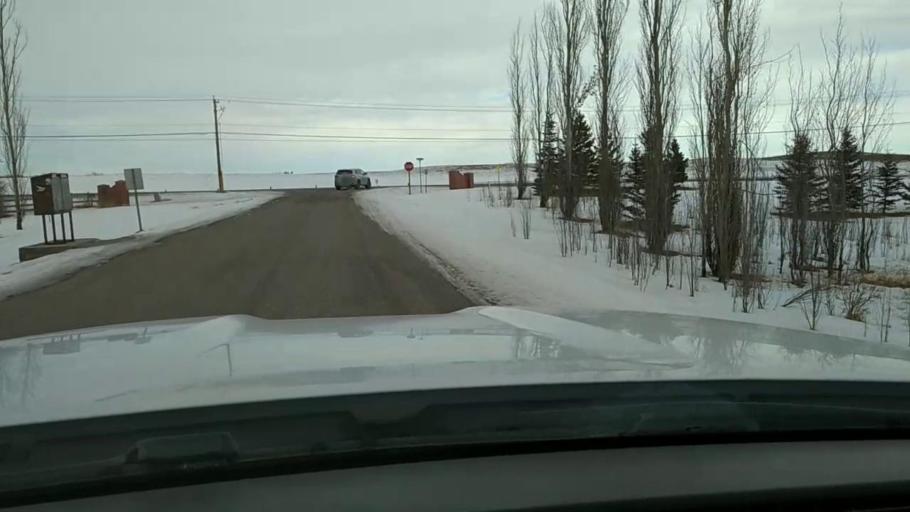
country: CA
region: Alberta
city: Calgary
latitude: 51.1826
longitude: -114.2486
